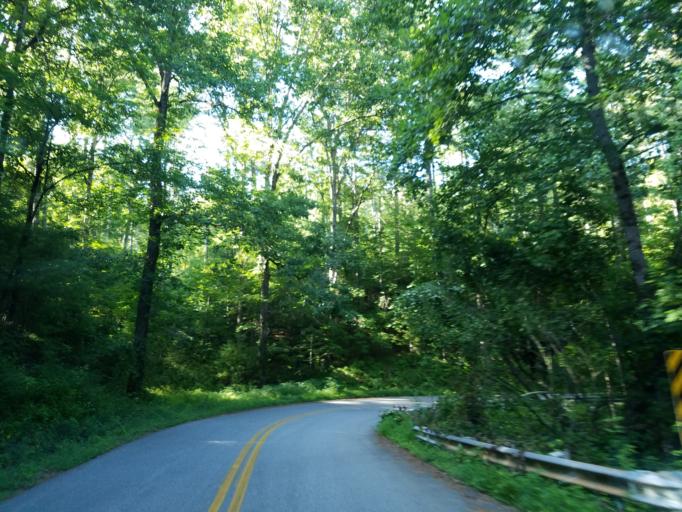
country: US
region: Georgia
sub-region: Union County
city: Blairsville
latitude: 34.7493
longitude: -84.1190
